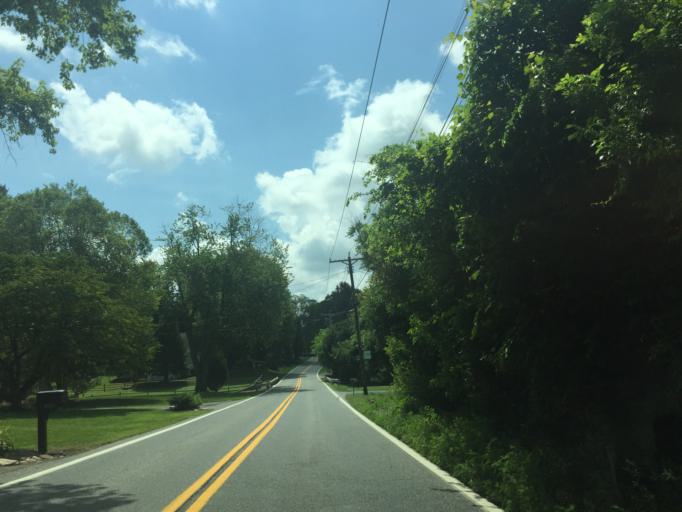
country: US
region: Maryland
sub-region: Baltimore County
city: Kingsville
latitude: 39.4470
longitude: -76.4175
